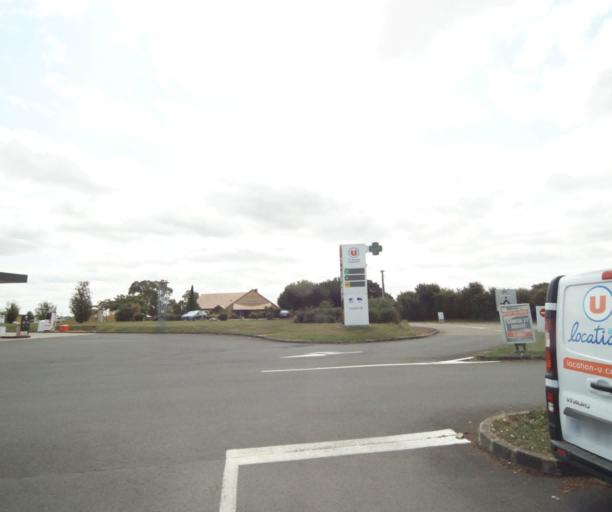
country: FR
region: Pays de la Loire
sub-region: Departement de la Sarthe
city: Sable-sur-Sarthe
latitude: 47.8509
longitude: -0.3524
